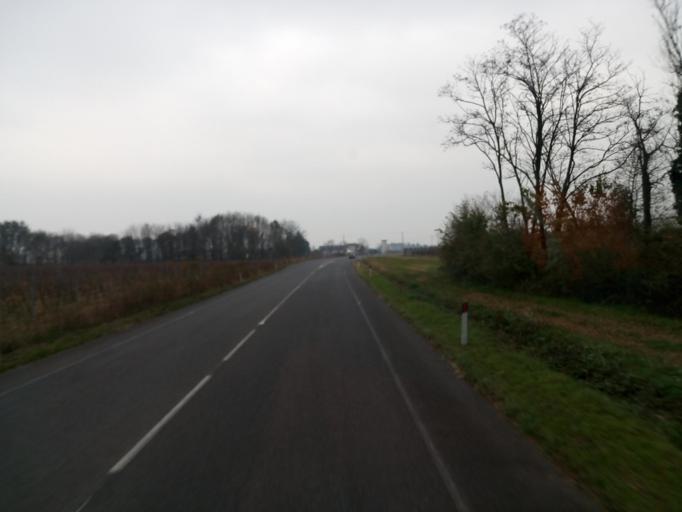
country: IT
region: Friuli Venezia Giulia
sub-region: Provincia di Udine
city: Buttrio
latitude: 46.0355
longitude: 13.3301
